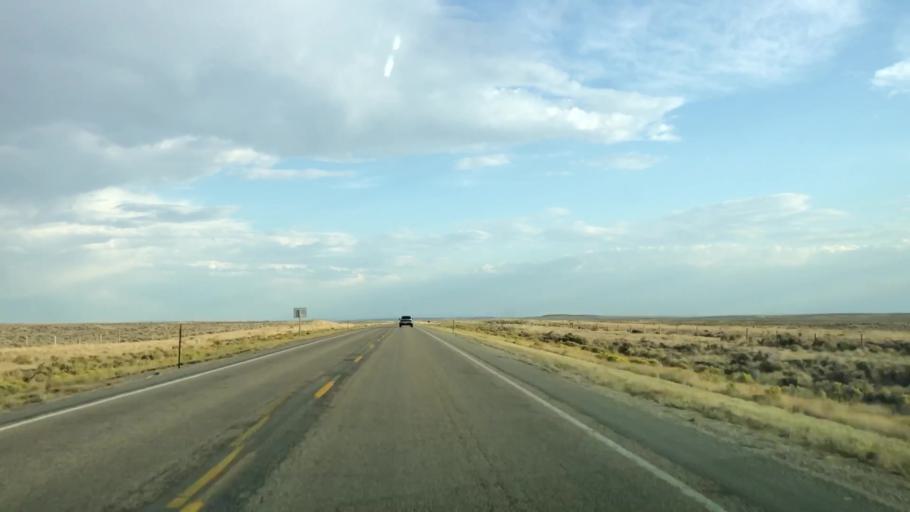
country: US
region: Wyoming
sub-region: Sublette County
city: Pinedale
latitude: 42.4078
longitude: -109.5507
